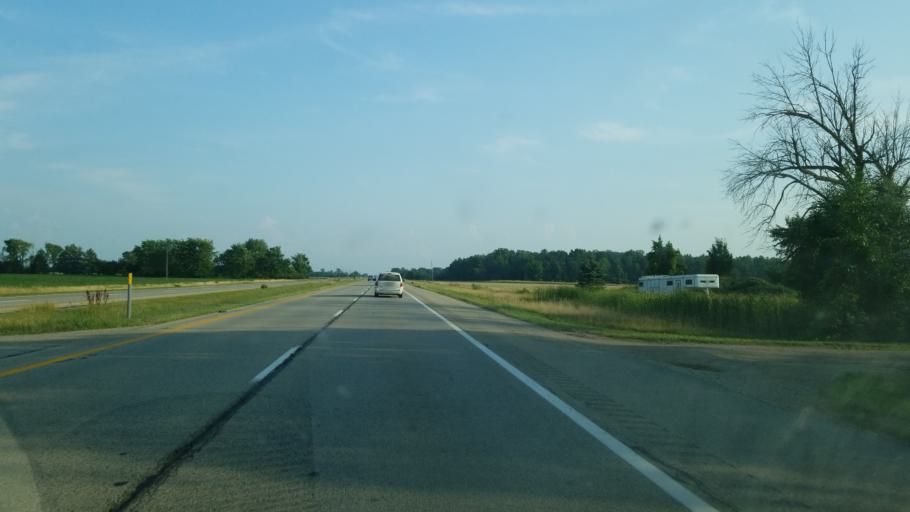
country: US
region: Michigan
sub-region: Gratiot County
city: Ithaca
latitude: 43.2009
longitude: -84.5635
